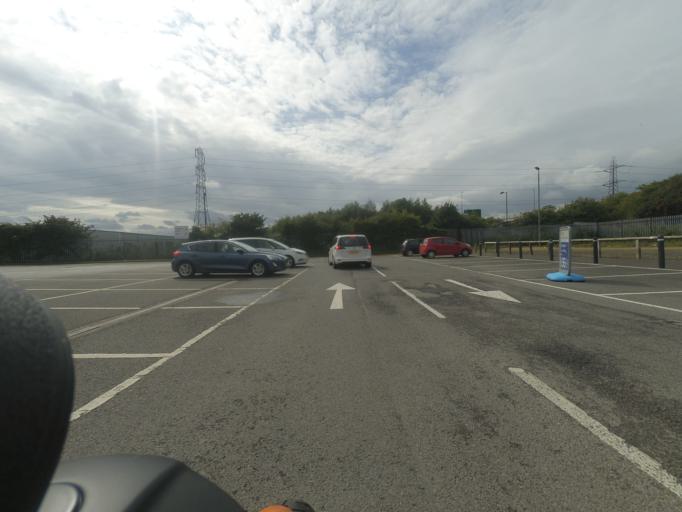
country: GB
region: England
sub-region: South Tyneside
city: Jarrow
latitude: 55.0106
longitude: -1.4875
